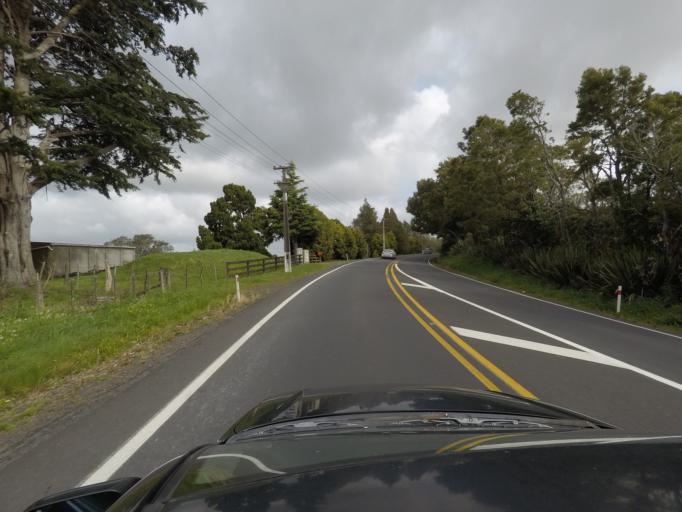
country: NZ
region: Auckland
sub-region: Auckland
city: Pakuranga
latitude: -36.9381
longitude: 174.9462
